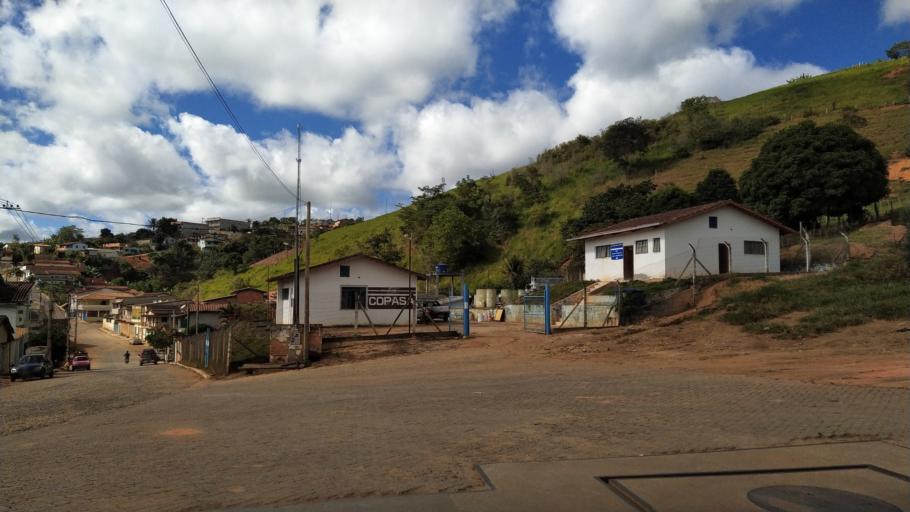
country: BR
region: Bahia
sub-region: Itanhem
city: Itanhem
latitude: -16.7357
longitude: -40.4261
